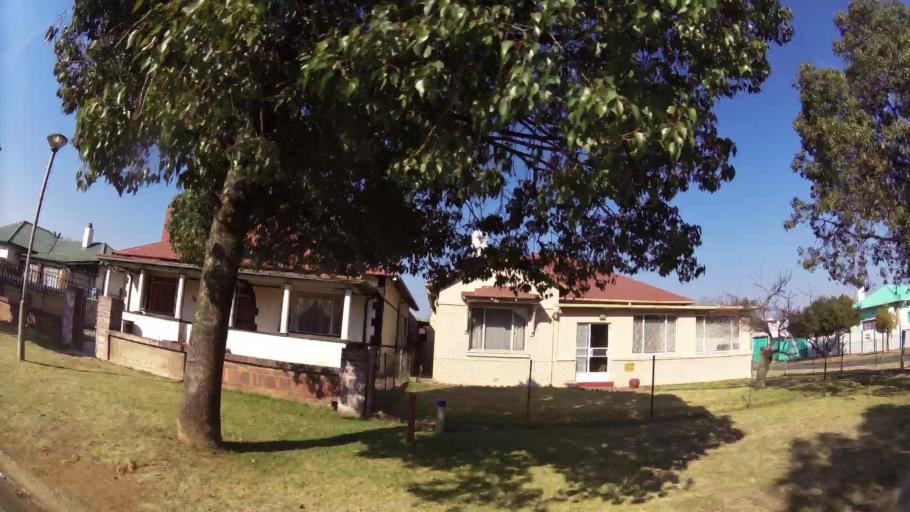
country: ZA
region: Gauteng
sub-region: Ekurhuleni Metropolitan Municipality
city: Boksburg
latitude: -26.2219
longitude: 28.2591
